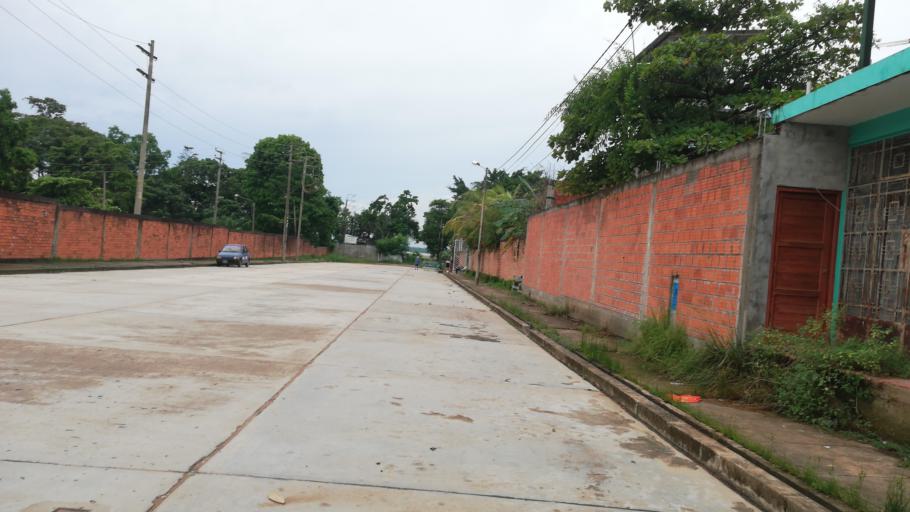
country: PE
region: Ucayali
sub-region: Provincia de Coronel Portillo
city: Puerto Callao
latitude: -8.3519
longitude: -74.5785
